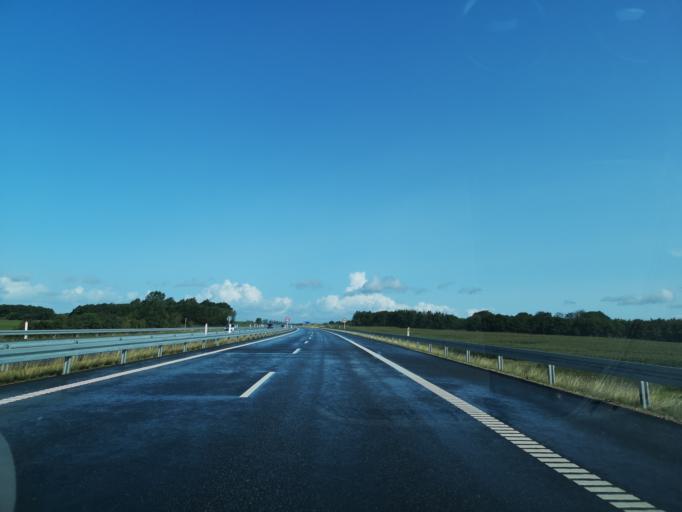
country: DK
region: Central Jutland
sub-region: Herning Kommune
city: Snejbjerg
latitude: 56.1779
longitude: 8.8927
